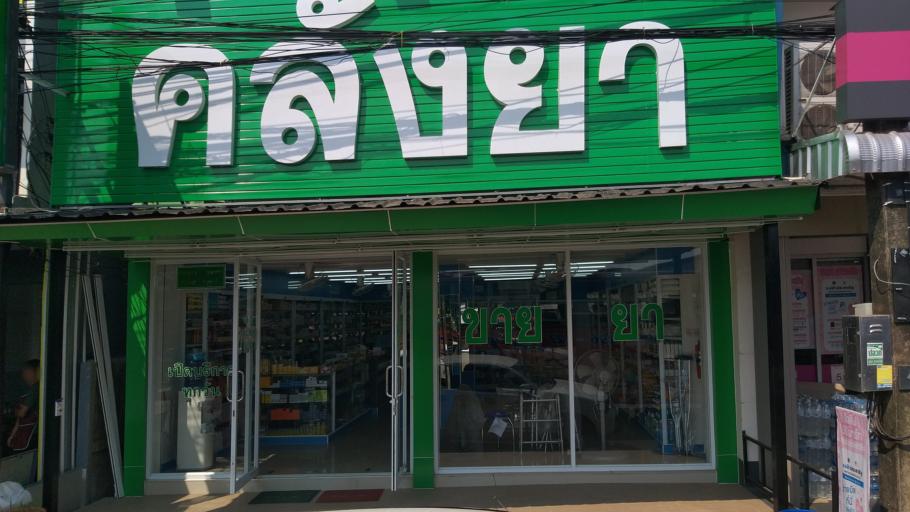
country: TH
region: Changwat Udon Thani
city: Nong Han
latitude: 17.3630
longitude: 103.1029
